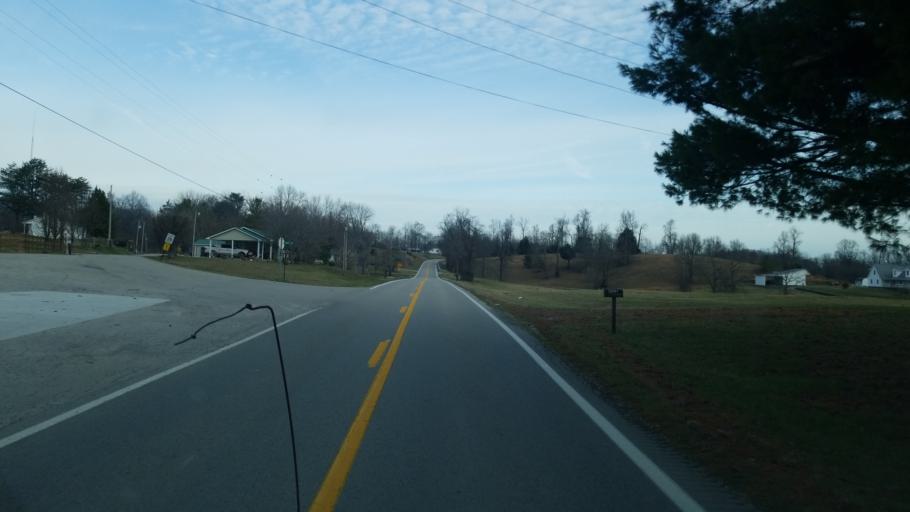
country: US
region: Kentucky
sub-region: Clinton County
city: Albany
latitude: 36.8008
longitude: -85.1810
